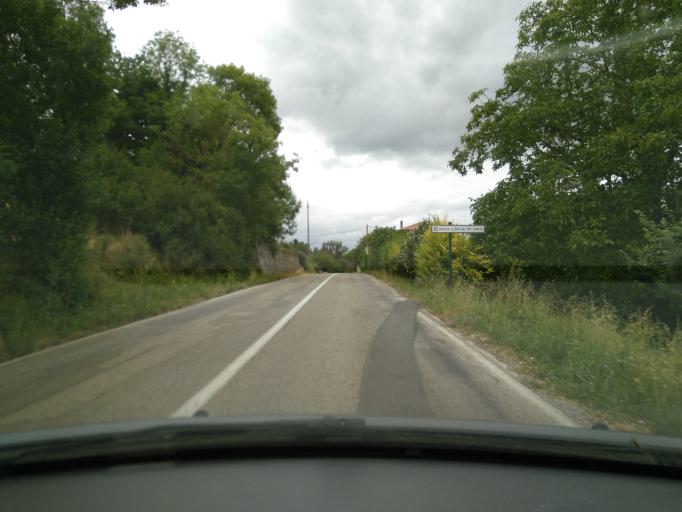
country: FR
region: Rhone-Alpes
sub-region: Departement de l'Isere
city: Champier
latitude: 45.4344
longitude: 5.2692
